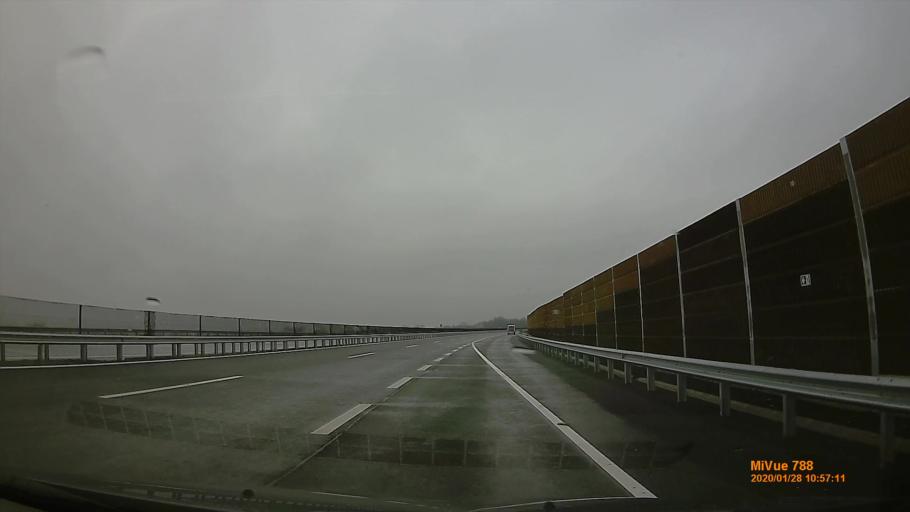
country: HU
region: Pest
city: Peteri
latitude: 47.3715
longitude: 19.4196
